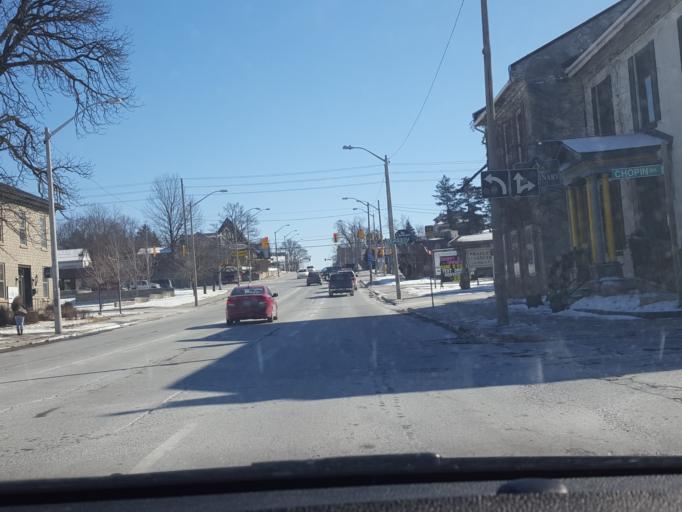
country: CA
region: Ontario
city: Cambridge
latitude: 43.3992
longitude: -80.3647
